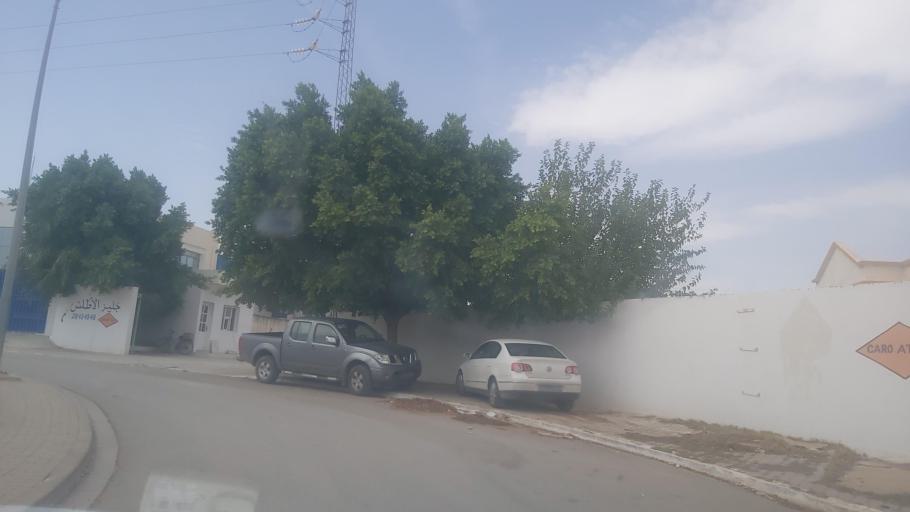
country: TN
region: Silyanah
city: Bu `Aradah
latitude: 36.3535
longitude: 9.6327
